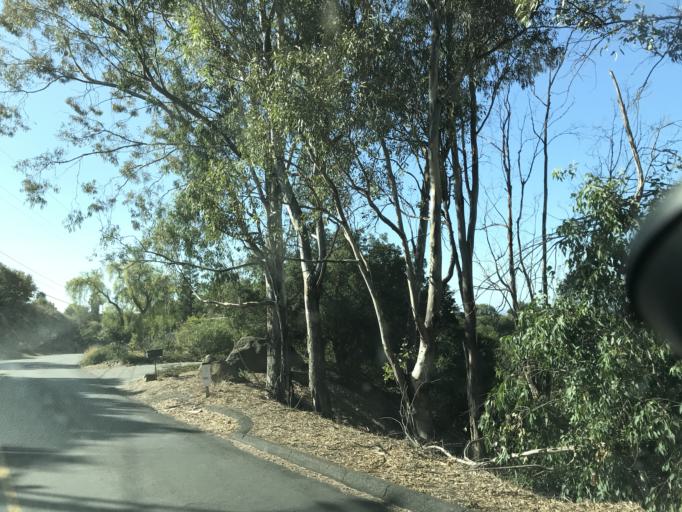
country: US
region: California
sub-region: Santa Barbara County
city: Goleta
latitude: 34.4685
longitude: -119.7753
